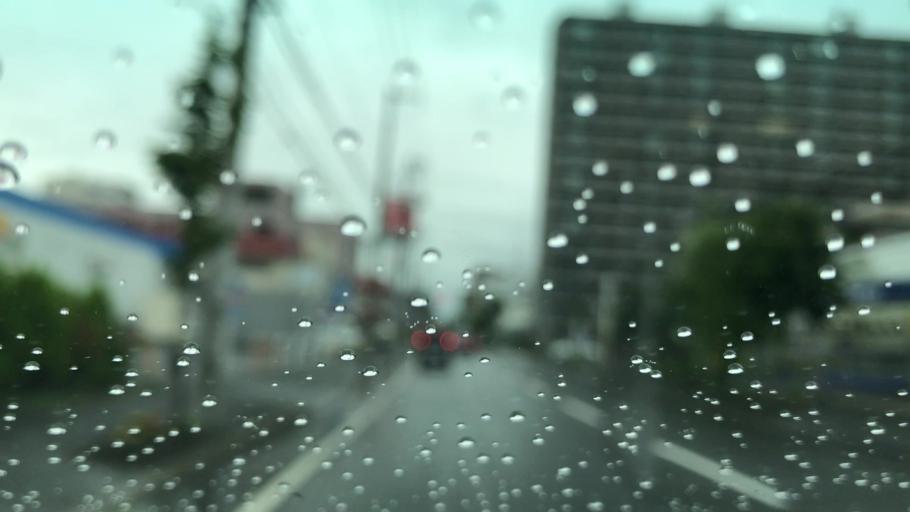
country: JP
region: Hokkaido
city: Sapporo
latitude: 43.0403
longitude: 141.3346
